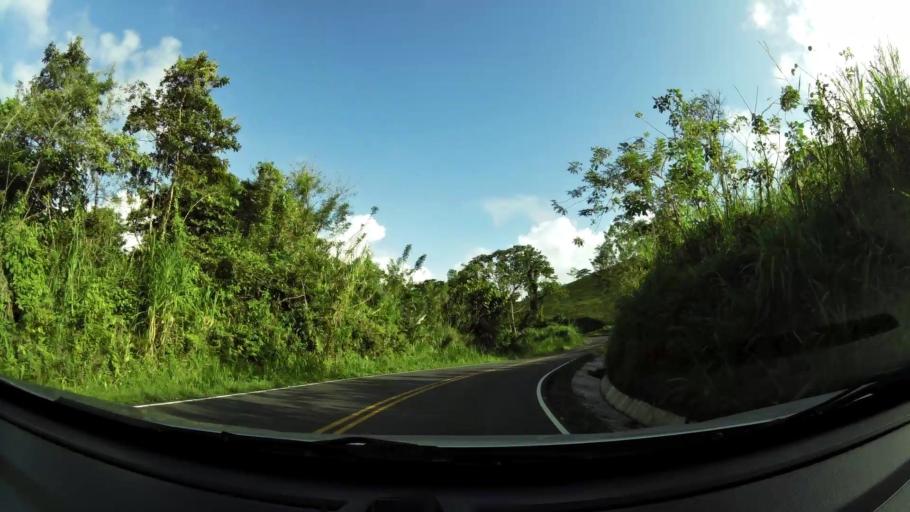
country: CR
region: Limon
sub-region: Canton de Siquirres
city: Siquirres
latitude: 10.0556
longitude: -83.5528
